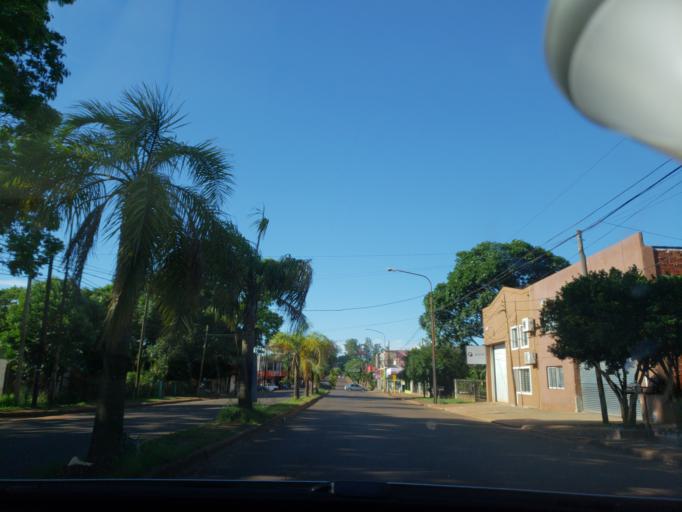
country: AR
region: Misiones
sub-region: Departamento de Capital
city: Posadas
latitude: -27.3999
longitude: -55.9210
